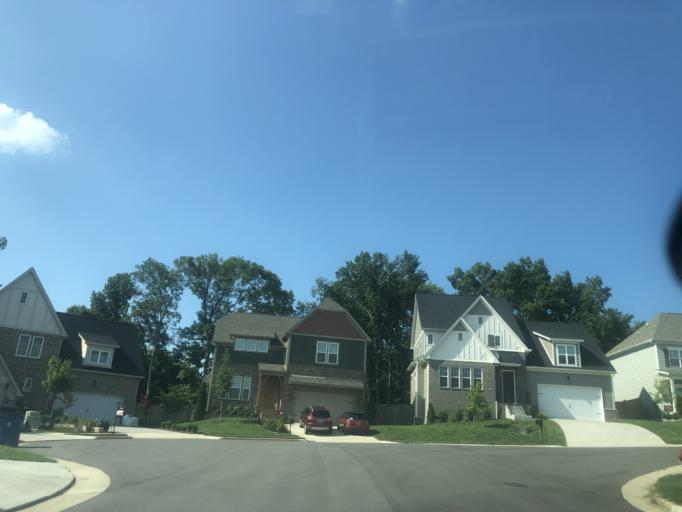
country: US
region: Tennessee
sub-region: Wilson County
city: Green Hill
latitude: 36.1501
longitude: -86.5895
